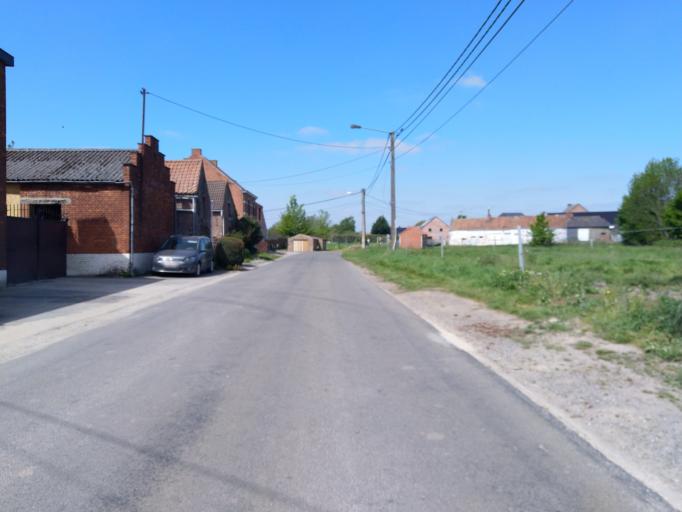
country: BE
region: Wallonia
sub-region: Province du Hainaut
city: Lens
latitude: 50.5287
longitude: 3.8517
